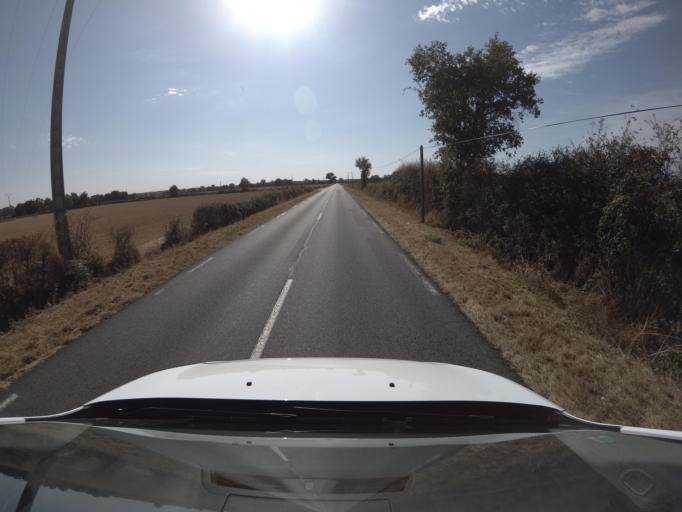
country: FR
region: Poitou-Charentes
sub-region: Departement des Deux-Sevres
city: Argenton-les-Vallees
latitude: 47.0028
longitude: -0.3655
